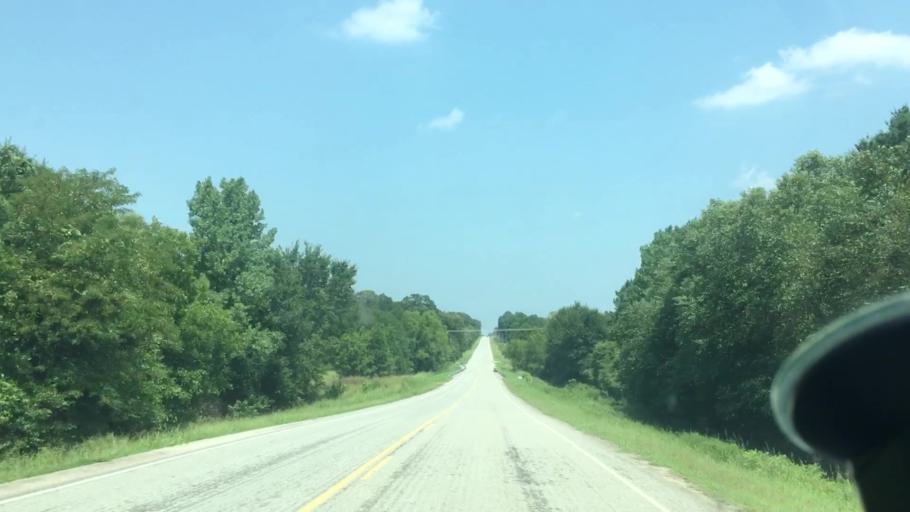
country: US
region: Oklahoma
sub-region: Atoka County
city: Atoka
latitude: 34.2554
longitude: -95.9361
